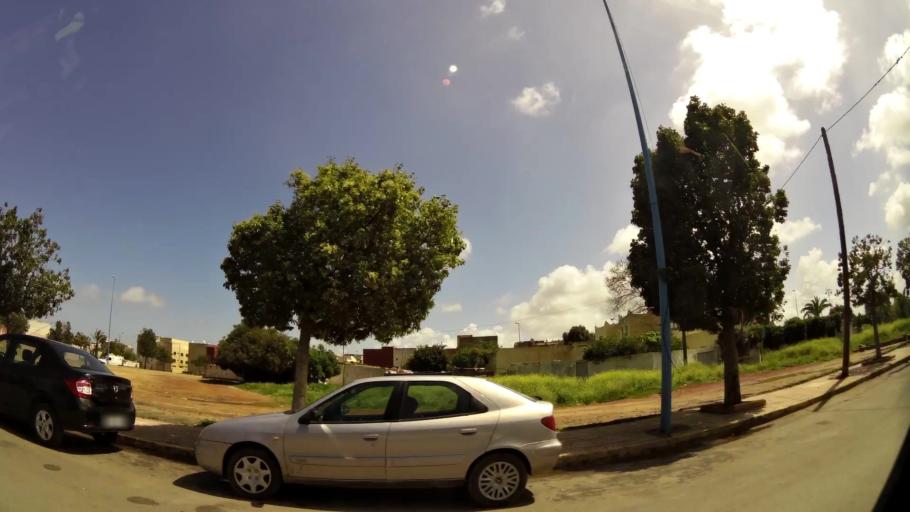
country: MA
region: Grand Casablanca
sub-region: Mediouna
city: Tit Mellil
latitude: 33.6352
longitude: -7.4546
